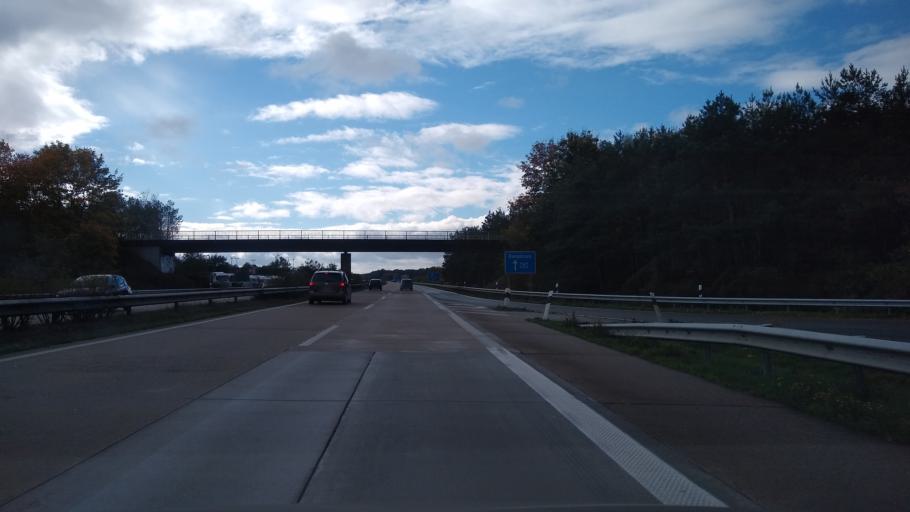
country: DE
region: Lower Saxony
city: Wardenburg
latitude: 53.0440
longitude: 8.2209
